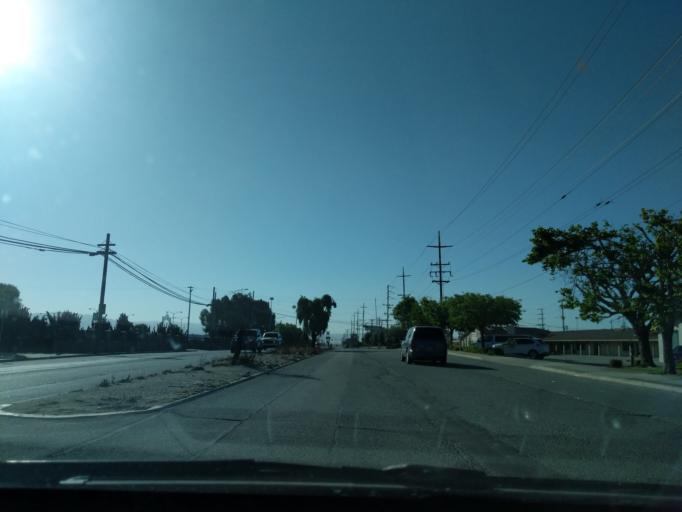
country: US
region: California
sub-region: Monterey County
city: Salinas
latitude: 36.6554
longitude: -121.6316
